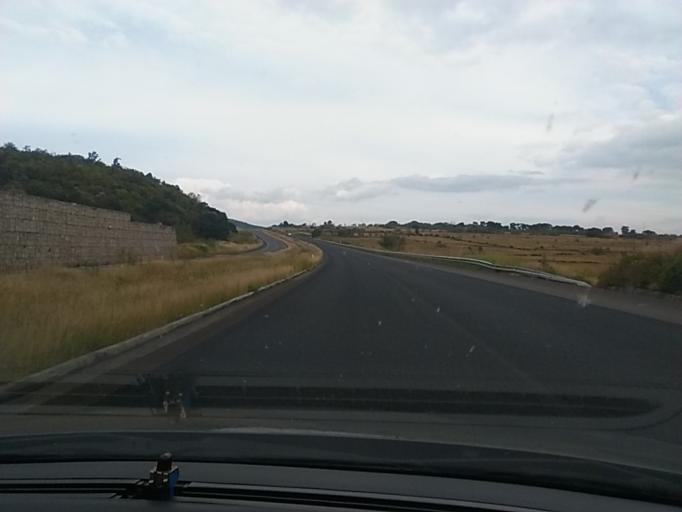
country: MX
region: Mexico
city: Huaniqueo de Morales
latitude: 19.8833
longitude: -101.4442
